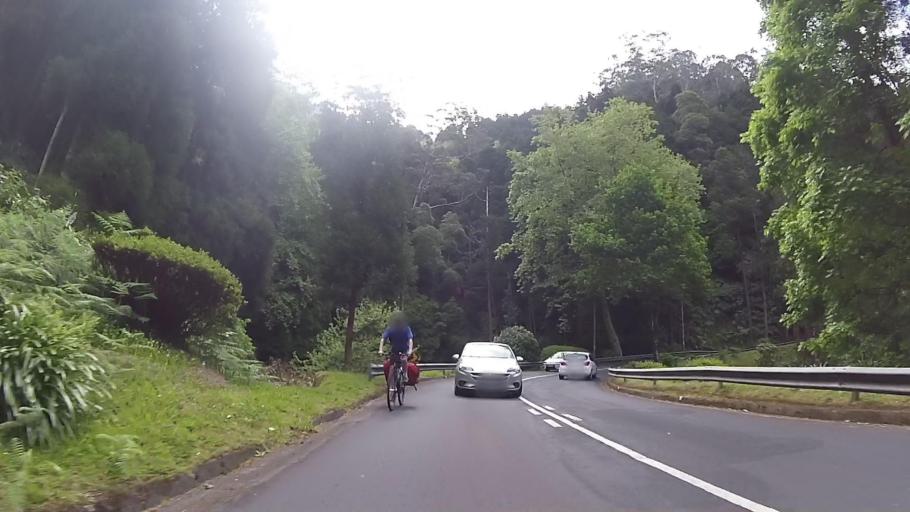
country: PT
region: Azores
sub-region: Povoacao
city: Furnas
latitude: 37.7637
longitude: -25.2863
